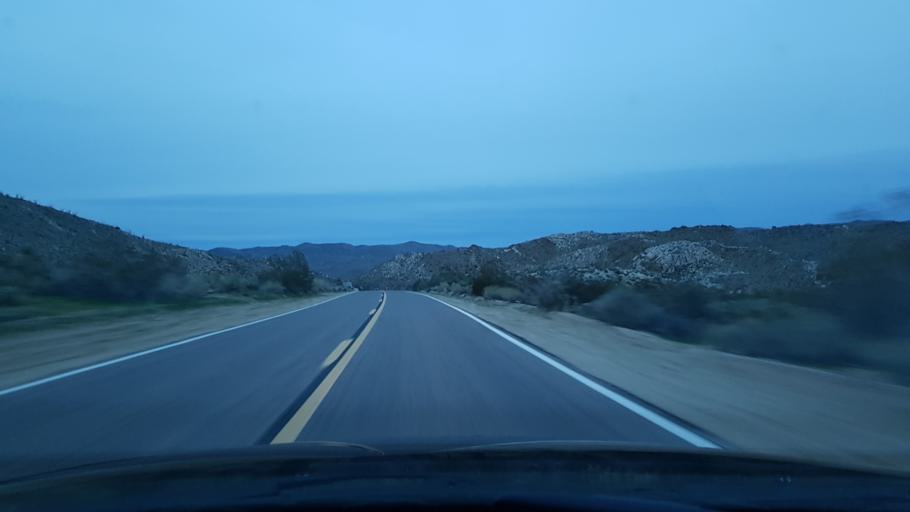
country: US
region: California
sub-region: San Diego County
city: Julian
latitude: 33.0333
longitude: -116.4124
